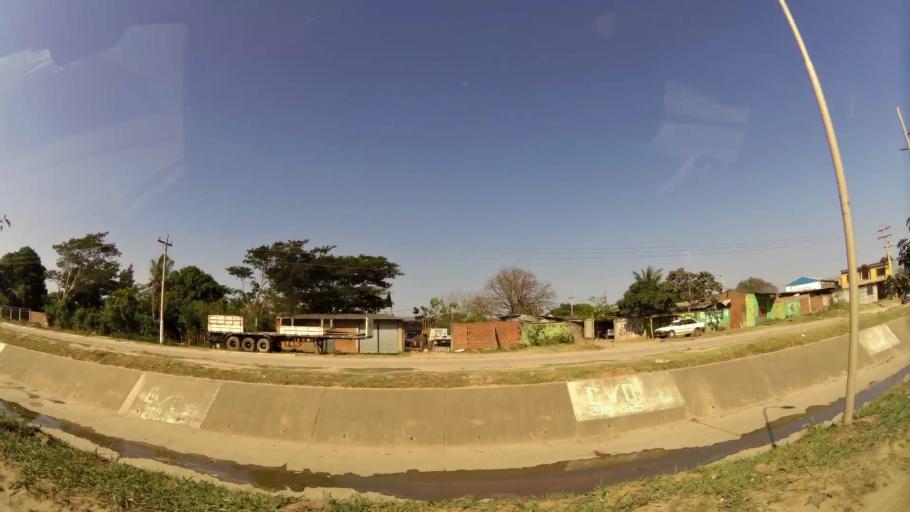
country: BO
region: Santa Cruz
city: Cotoca
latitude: -17.8123
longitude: -63.1098
